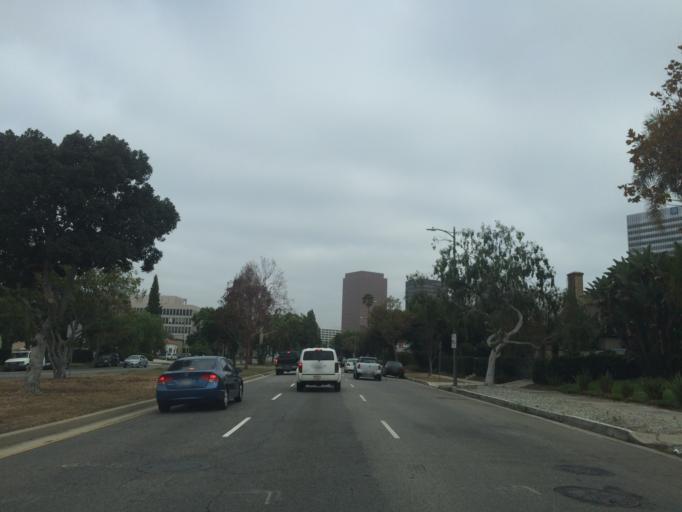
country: US
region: California
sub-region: Los Angeles County
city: West Hollywood
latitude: 34.0595
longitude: -118.3647
